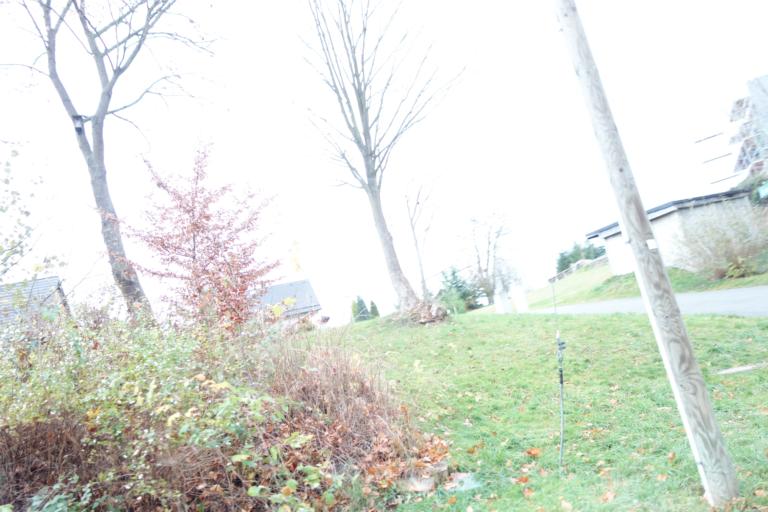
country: DE
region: Saxony
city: Eppendorf
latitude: 50.8141
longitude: 13.2551
